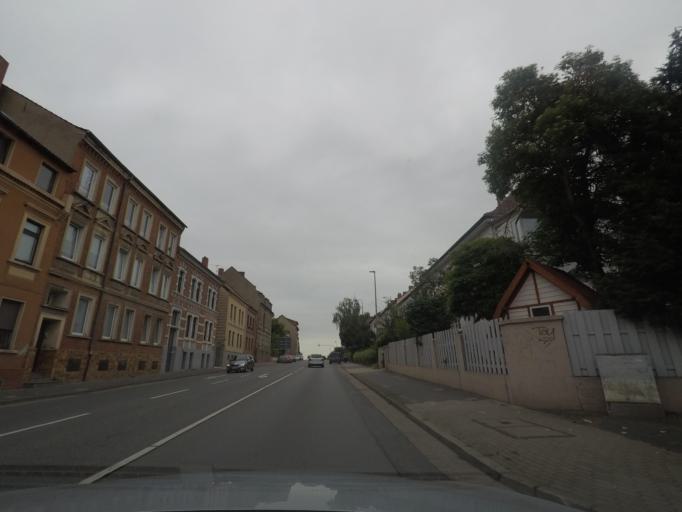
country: DE
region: Lower Saxony
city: Schoningen
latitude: 52.1395
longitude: 10.9680
